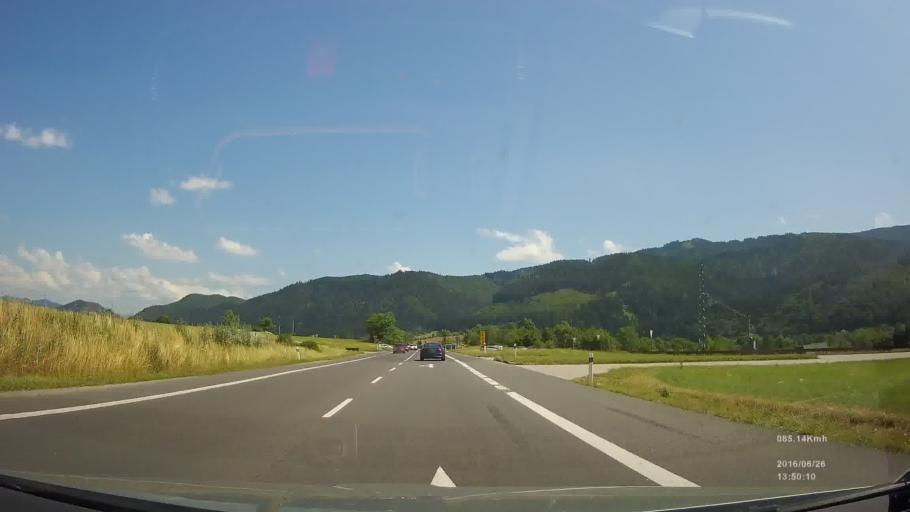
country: SK
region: Banskobystricky
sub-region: Okres Banska Bystrica
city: Brezno
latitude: 48.8132
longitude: 19.4494
